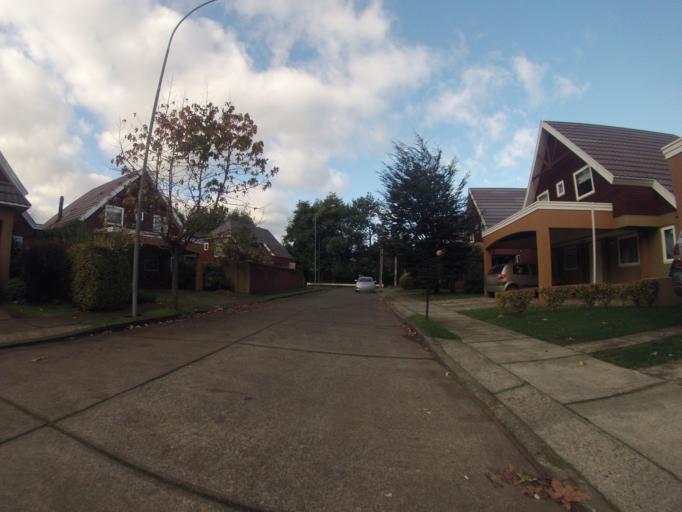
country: CL
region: Araucania
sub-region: Provincia de Cautin
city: Temuco
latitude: -38.7358
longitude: -72.6464
